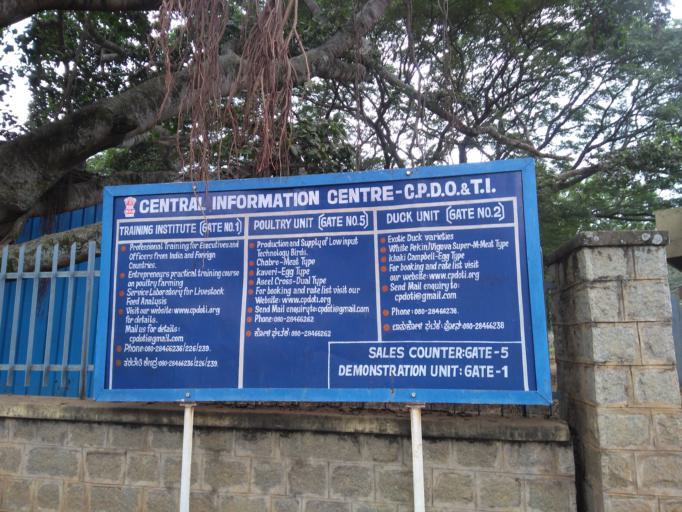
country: IN
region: Karnataka
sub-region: Bangalore Rural
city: Nelamangala
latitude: 13.1495
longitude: 77.4765
